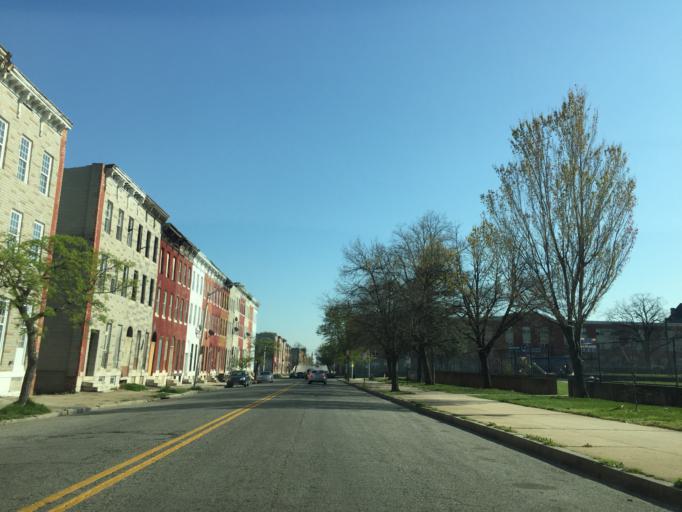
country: US
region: Maryland
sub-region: City of Baltimore
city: Baltimore
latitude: 39.2966
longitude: -76.6400
